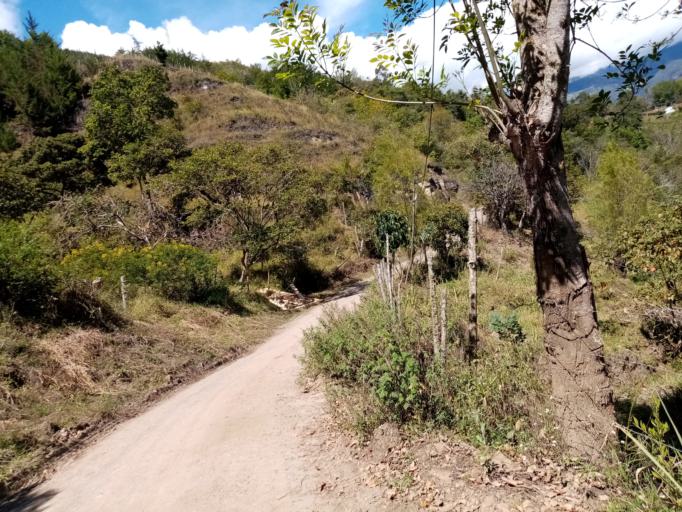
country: CO
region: Cundinamarca
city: Tenza
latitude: 5.0763
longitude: -73.4330
